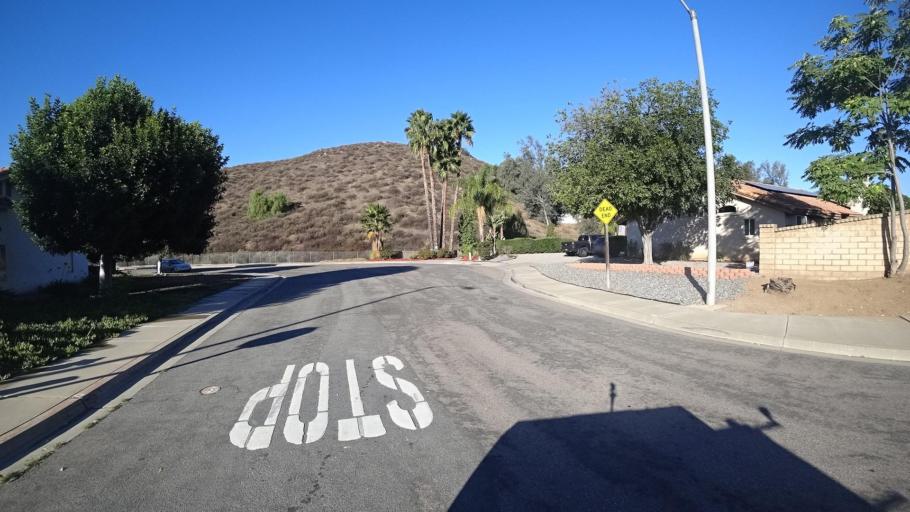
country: US
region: California
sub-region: San Diego County
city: Lakeside
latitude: 32.8423
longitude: -116.9156
